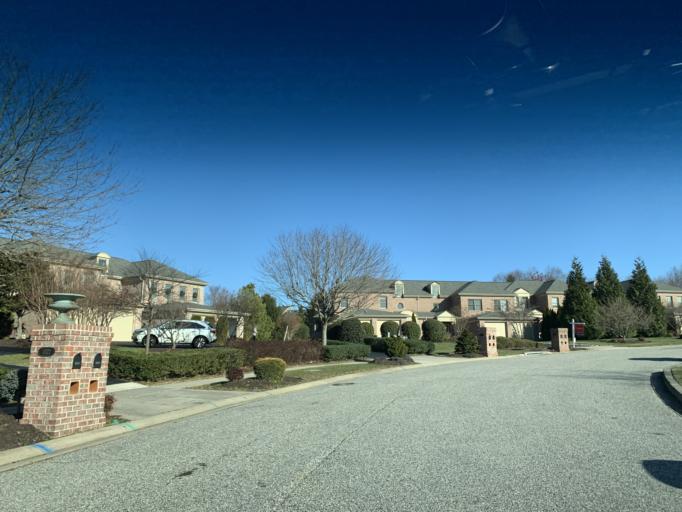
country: US
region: Maryland
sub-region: Harford County
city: Bel Air South
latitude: 39.5134
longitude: -76.3027
